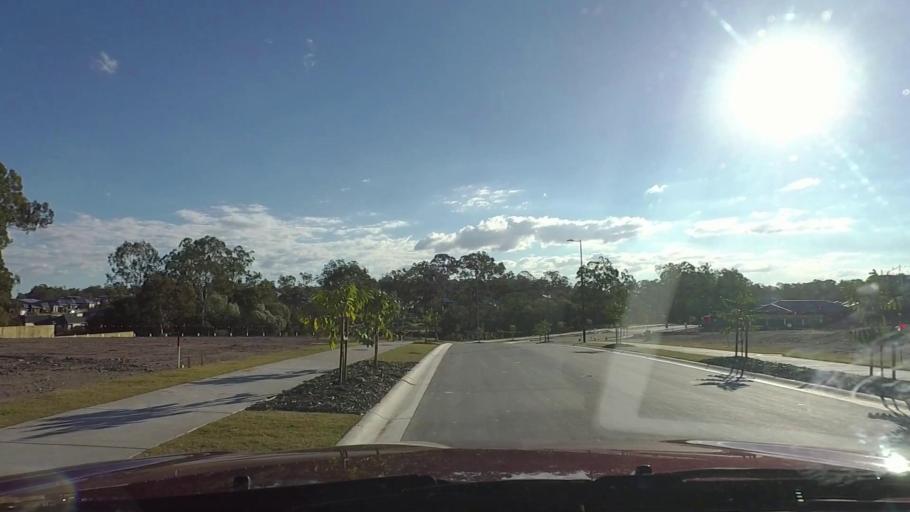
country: AU
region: Queensland
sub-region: Logan
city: Windaroo
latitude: -27.7315
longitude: 153.1688
